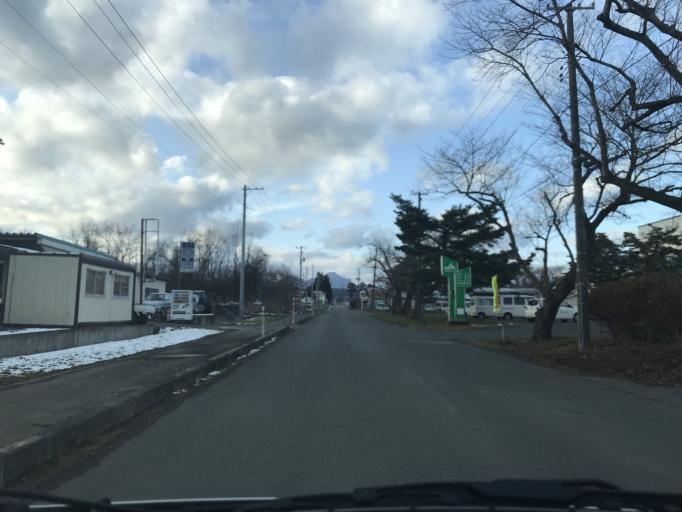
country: JP
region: Iwate
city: Kitakami
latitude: 39.2045
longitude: 141.0498
